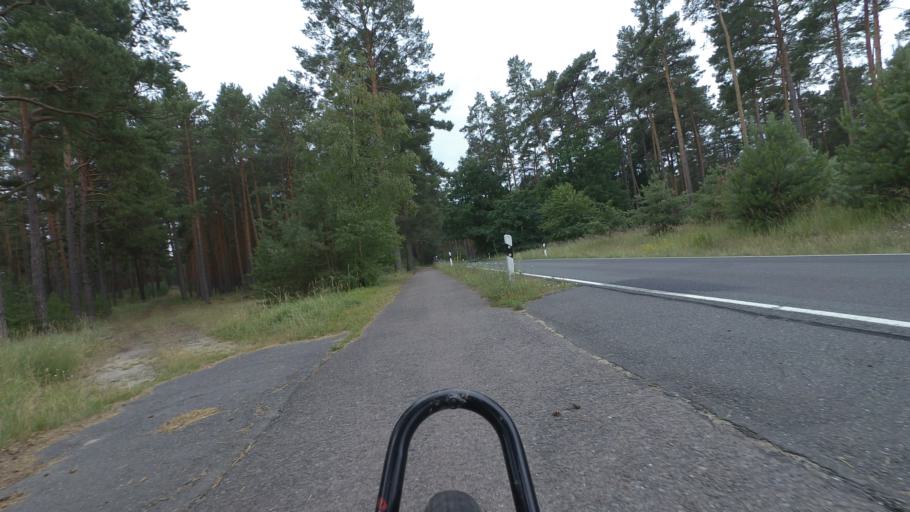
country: DE
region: Brandenburg
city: Beelitz
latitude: 52.1424
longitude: 13.0476
